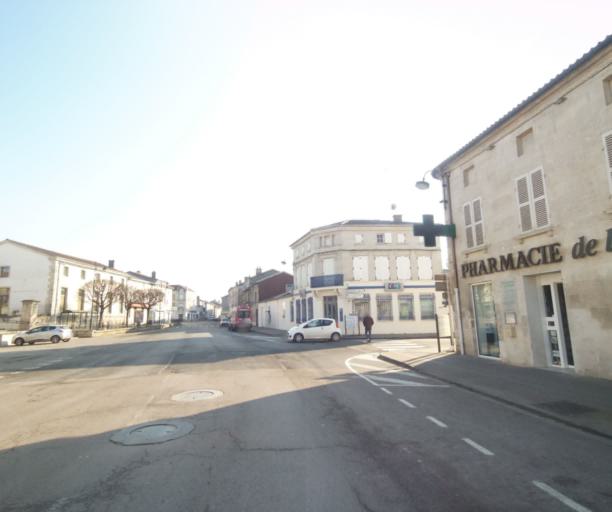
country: FR
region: Champagne-Ardenne
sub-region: Departement de la Haute-Marne
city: Wassy
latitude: 48.4981
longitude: 4.9480
